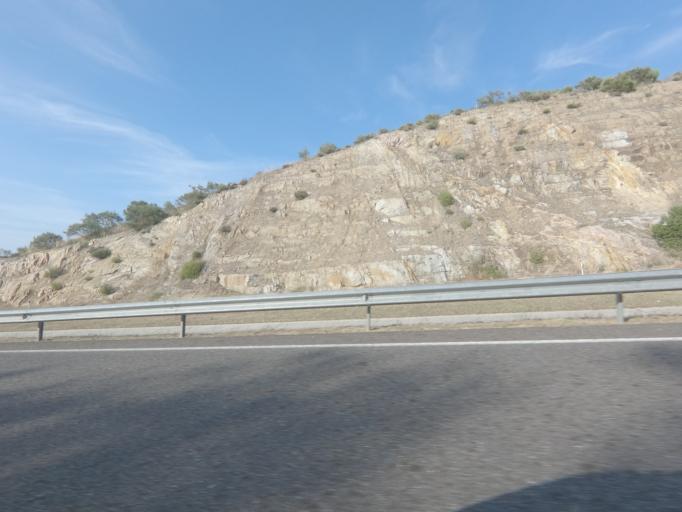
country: ES
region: Galicia
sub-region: Provincia de Ourense
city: Oimbra
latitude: 41.8614
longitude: -7.4265
